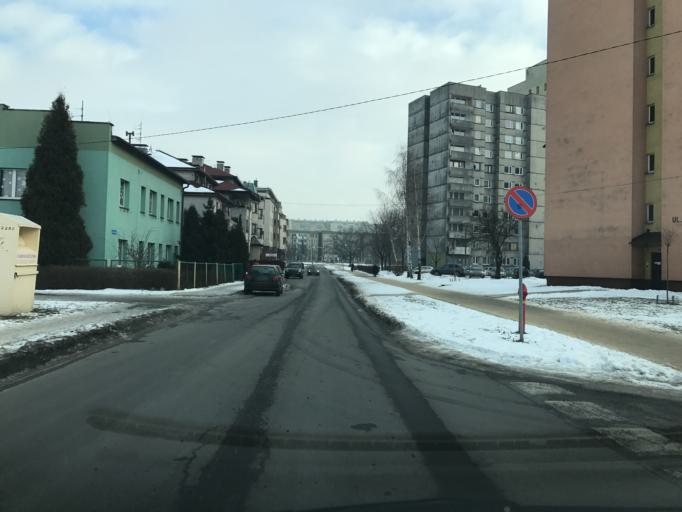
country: PL
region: Silesian Voivodeship
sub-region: Tychy
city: Tychy
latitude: 50.1140
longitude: 18.9775
